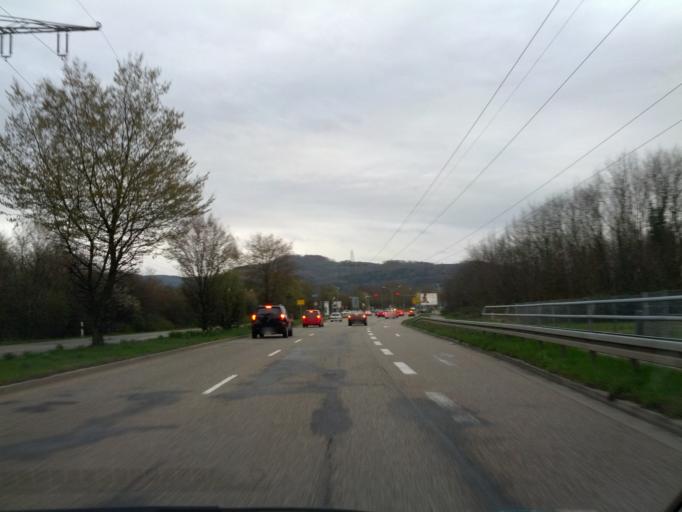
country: DE
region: Baden-Wuerttemberg
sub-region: Freiburg Region
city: Ebringen
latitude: 47.9973
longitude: 7.7991
